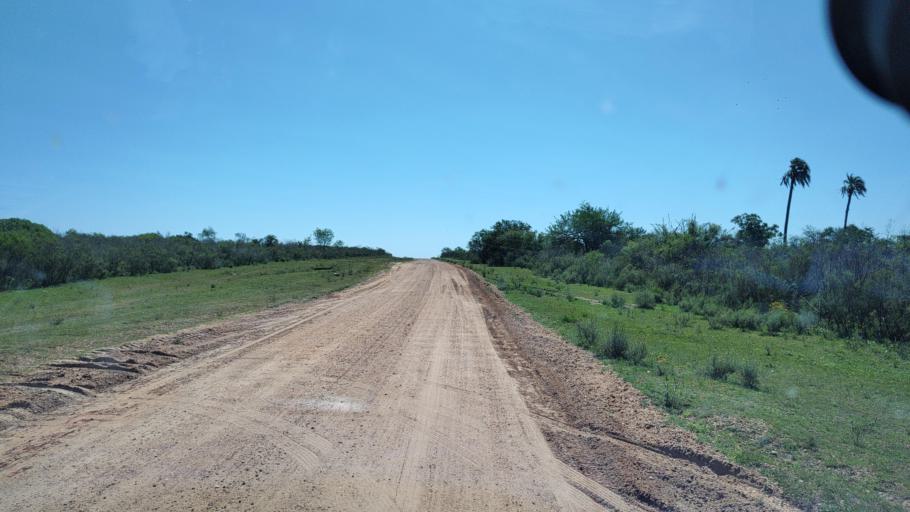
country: AR
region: Entre Rios
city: Ubajay
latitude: -31.8686
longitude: -58.2463
